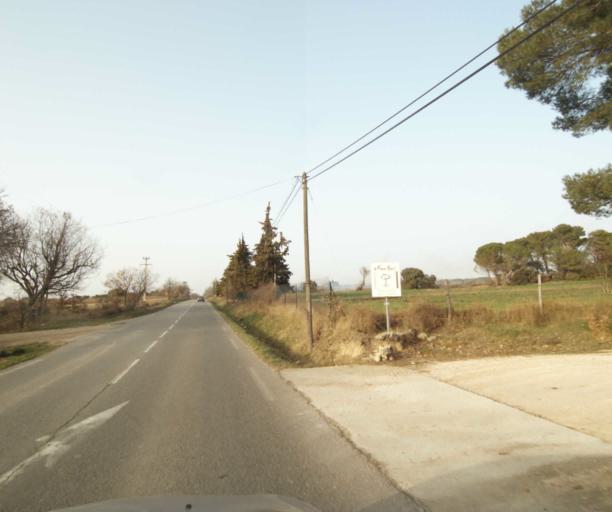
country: FR
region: Provence-Alpes-Cote d'Azur
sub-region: Departement des Bouches-du-Rhone
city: Eguilles
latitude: 43.5939
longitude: 5.3666
